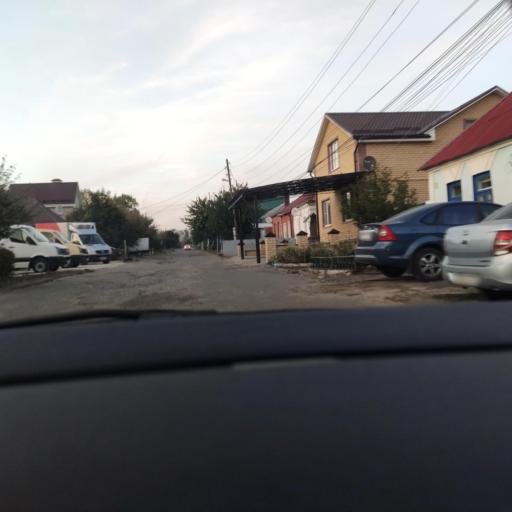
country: RU
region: Voronezj
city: Podgornoye
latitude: 51.6952
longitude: 39.1513
